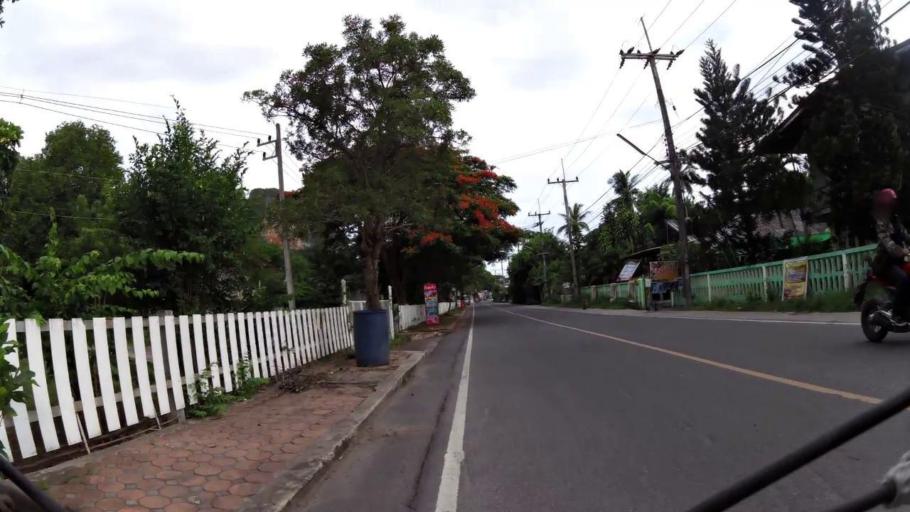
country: TH
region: Prachuap Khiri Khan
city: Prachuap Khiri Khan
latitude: 11.7496
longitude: 99.7899
